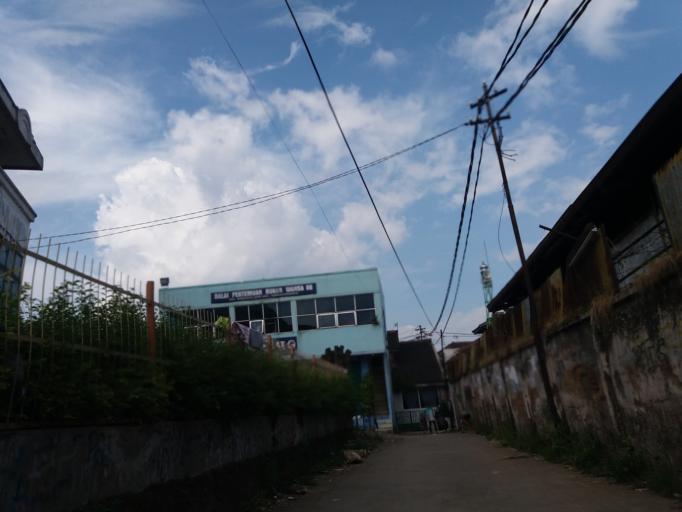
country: ID
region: West Java
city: Bandung
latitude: -6.9225
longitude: 107.6450
